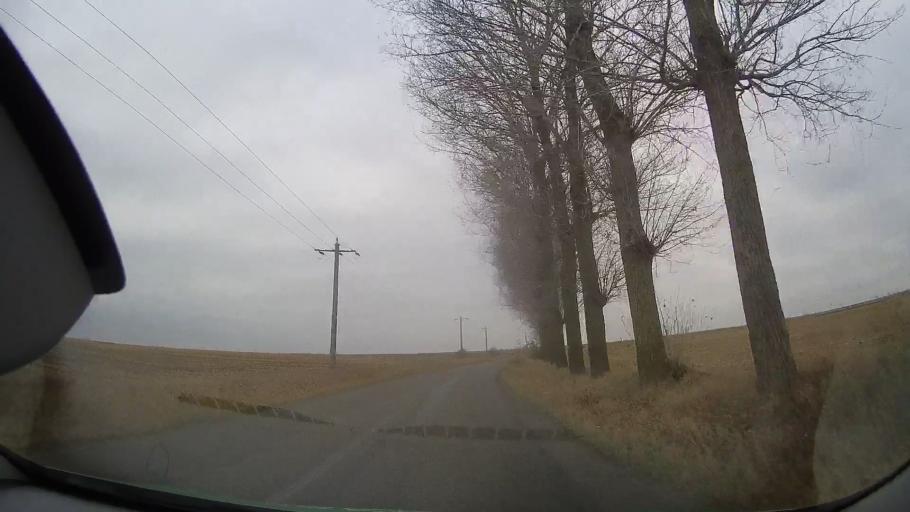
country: RO
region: Buzau
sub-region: Comuna Pogoanele
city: Pogoanele
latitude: 44.9540
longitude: 27.0173
